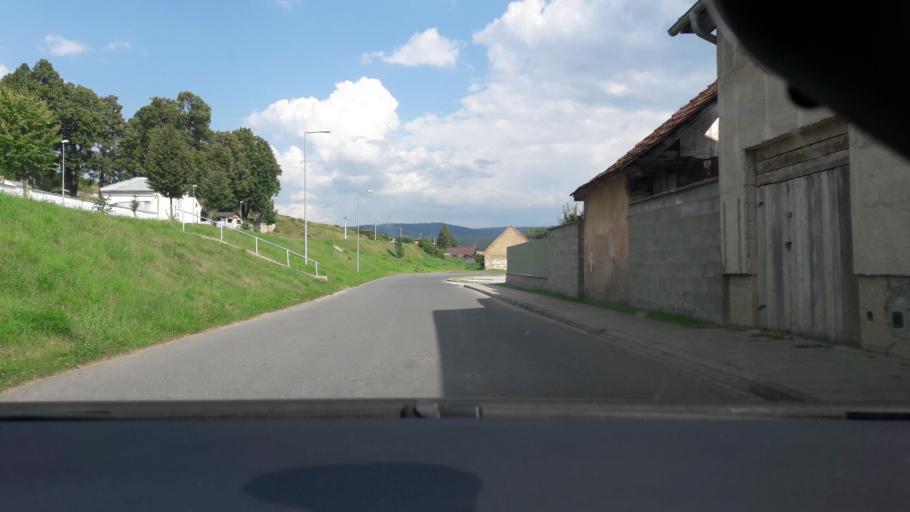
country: SK
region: Presovsky
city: Lubica
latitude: 49.1203
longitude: 20.4525
